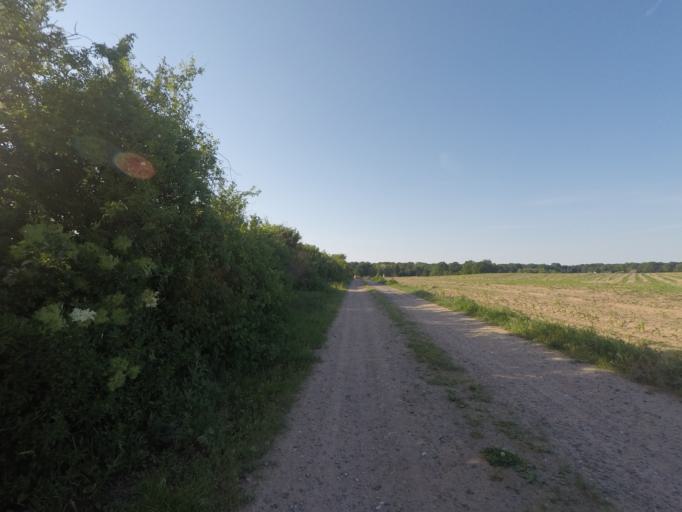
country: DE
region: Brandenburg
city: Joachimsthal
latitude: 52.9010
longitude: 13.7030
